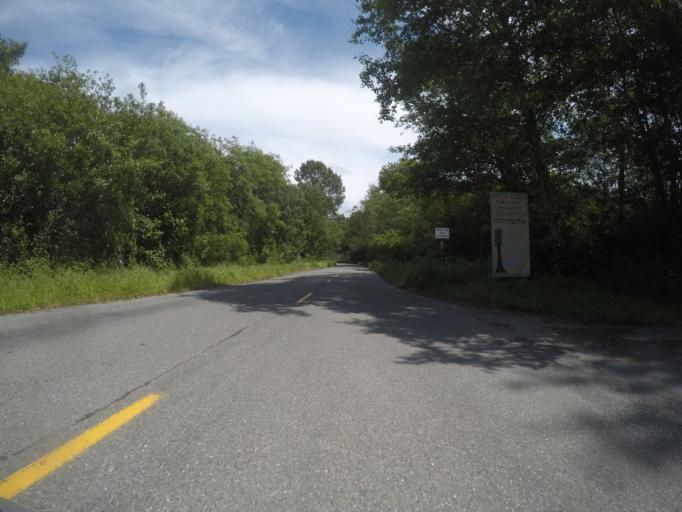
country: US
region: California
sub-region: Humboldt County
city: Westhaven-Moonstone
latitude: 41.3010
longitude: -124.0464
